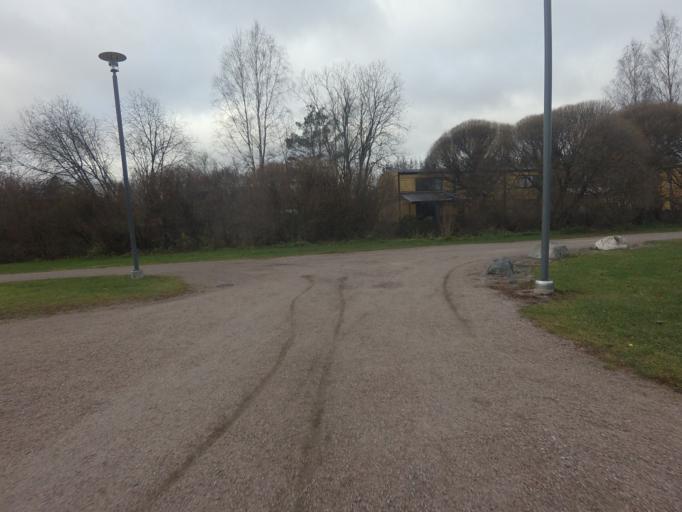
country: FI
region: Uusimaa
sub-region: Helsinki
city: Espoo
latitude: 60.1975
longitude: 24.6770
